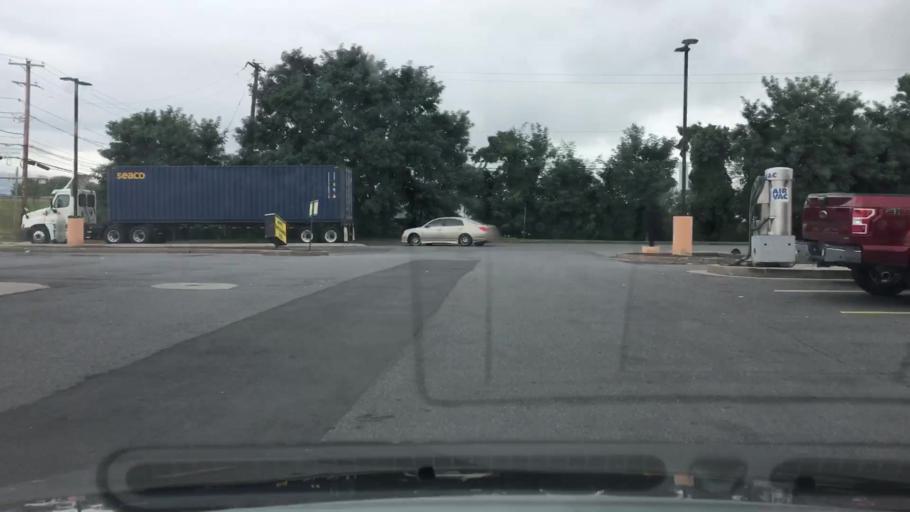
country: US
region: Pennsylvania
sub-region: Luzerne County
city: Dupont
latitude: 41.3143
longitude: -75.7552
